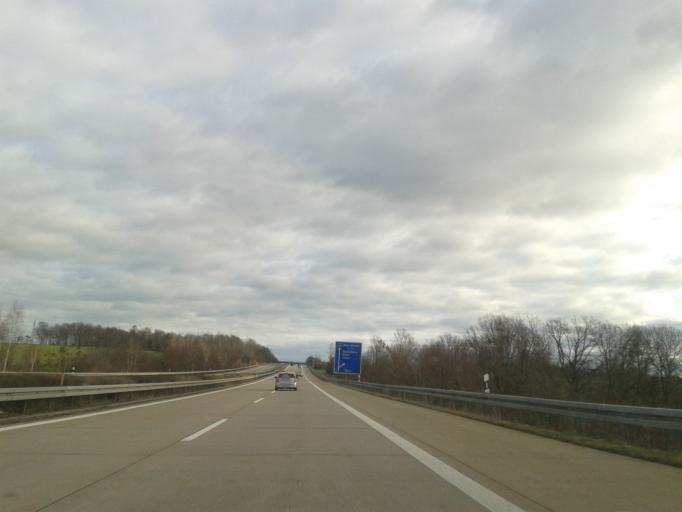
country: DE
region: Saxony
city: Weissenberg
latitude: 51.2067
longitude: 14.6491
